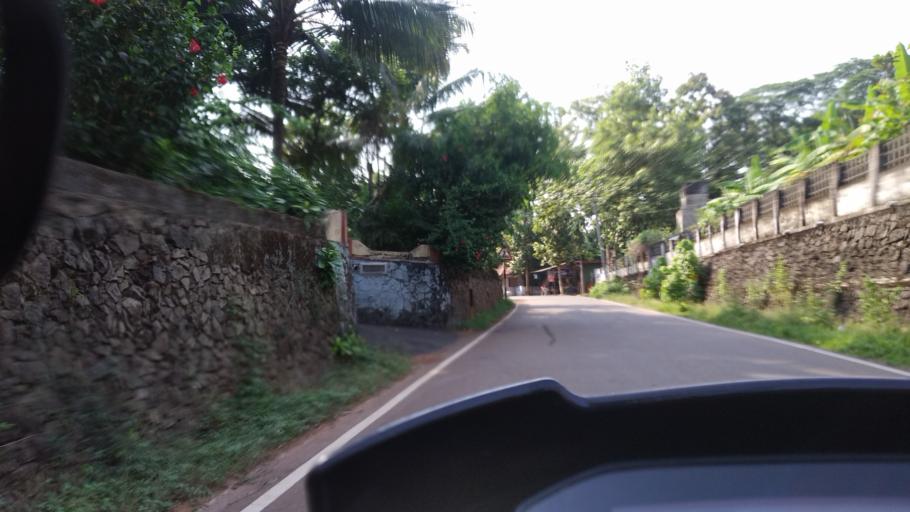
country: IN
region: Kerala
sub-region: Ernakulam
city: Piravam
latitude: 9.8561
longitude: 76.5236
